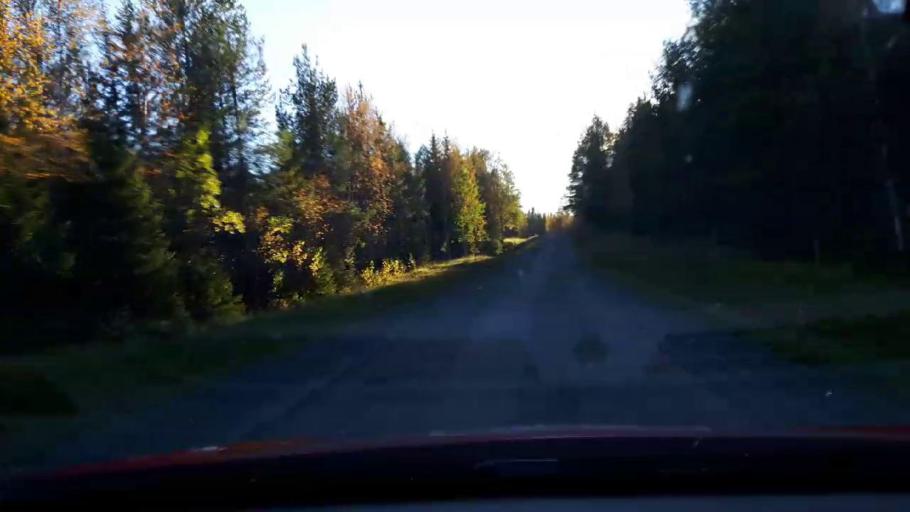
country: SE
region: Jaemtland
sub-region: OEstersunds Kommun
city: Lit
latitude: 63.4122
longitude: 14.6658
